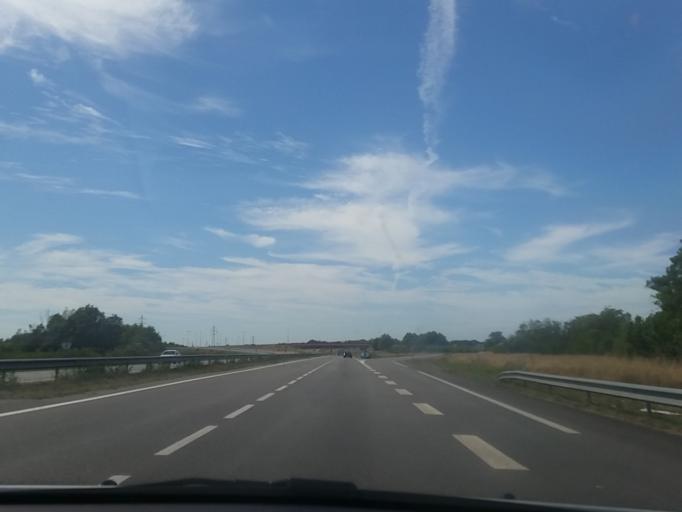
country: FR
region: Pays de la Loire
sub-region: Departement de la Loire-Atlantique
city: Saint-Jean-de-Boiseau
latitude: 47.1820
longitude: -1.7190
